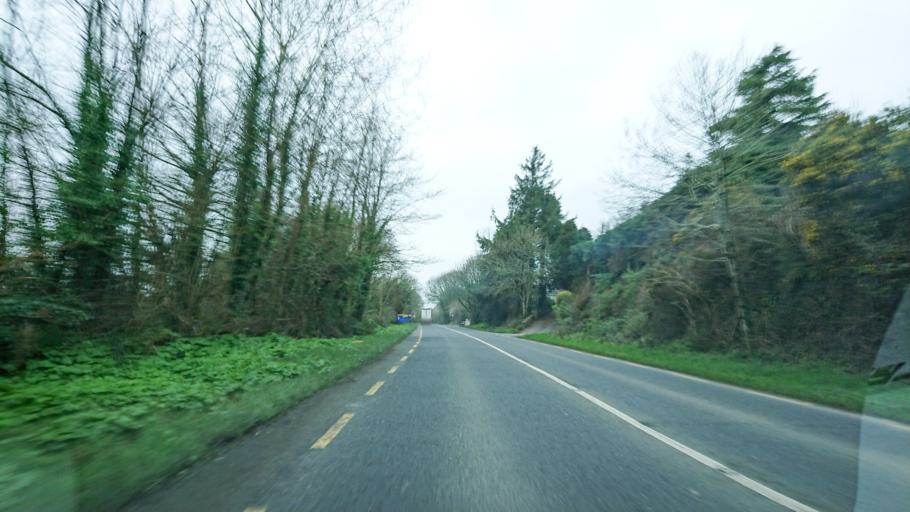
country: IE
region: Munster
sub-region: County Cork
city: Bandon
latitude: 51.7467
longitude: -8.7606
